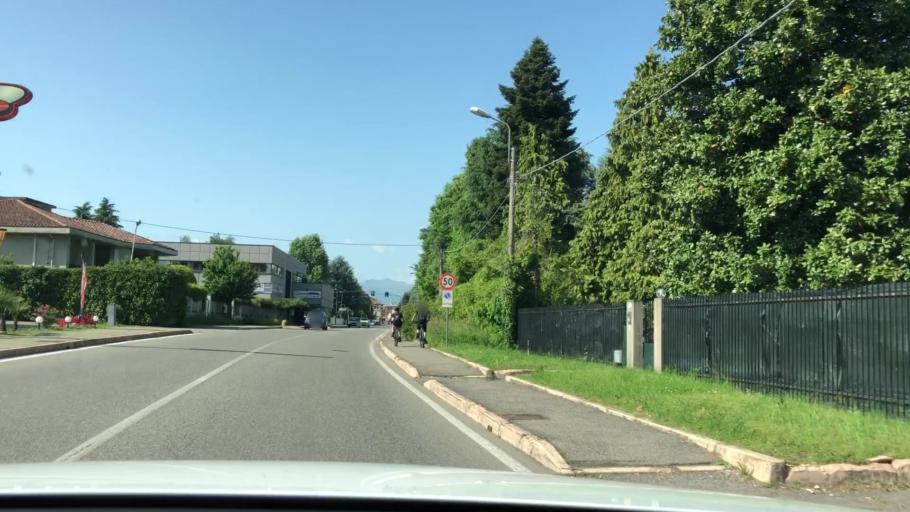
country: IT
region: Lombardy
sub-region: Provincia di Como
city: Cadorago-Caslino al Piano
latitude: 45.7177
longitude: 9.0390
